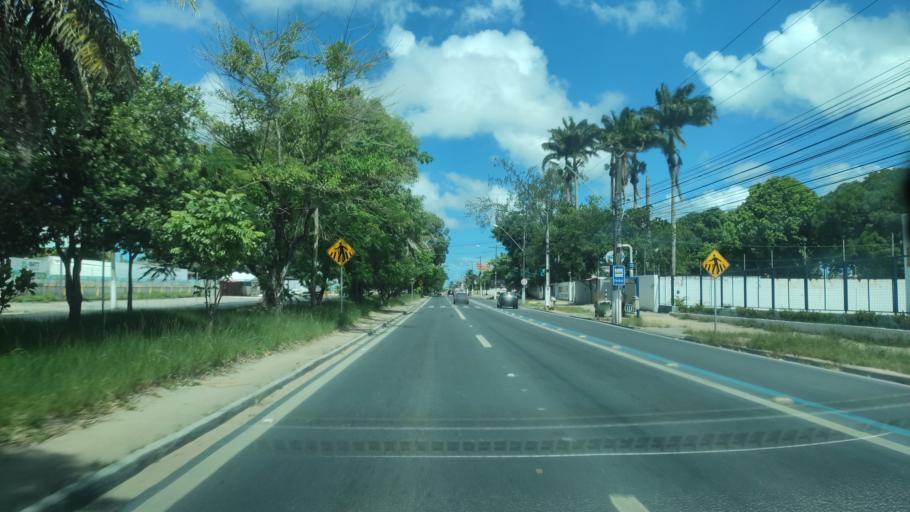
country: BR
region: Alagoas
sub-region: Satuba
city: Satuba
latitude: -9.5821
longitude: -35.7663
